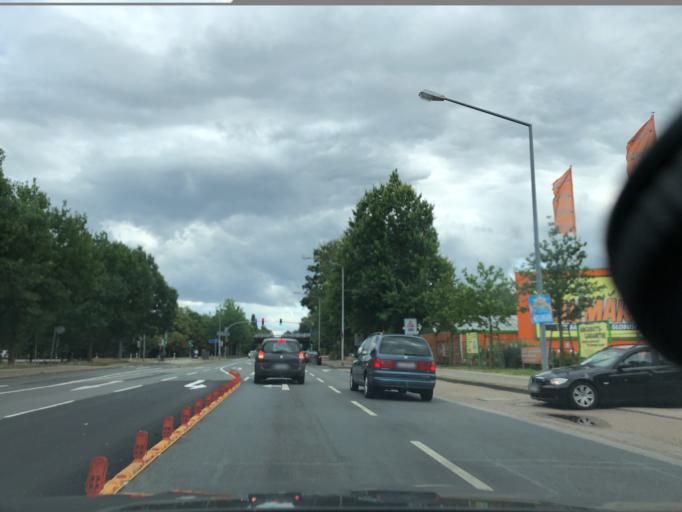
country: DE
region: Lower Saxony
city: Oldenburg
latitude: 53.1594
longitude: 8.1681
